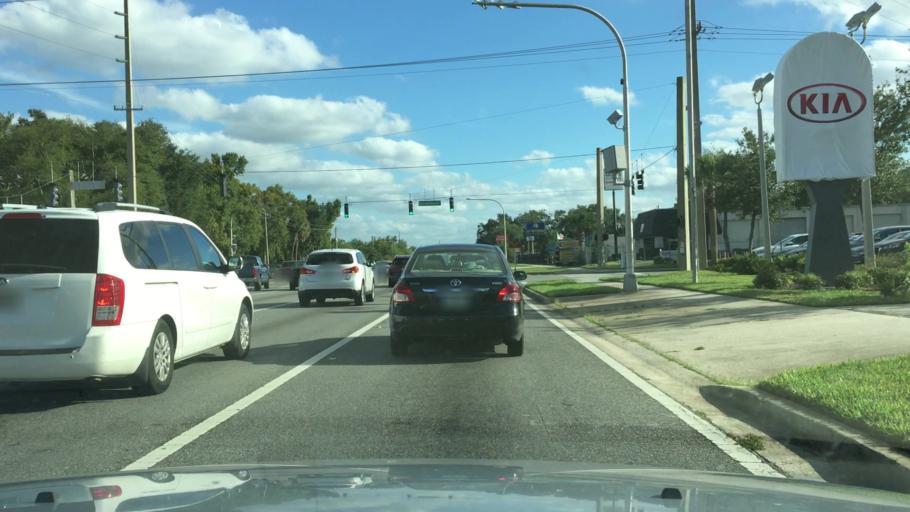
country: US
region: Florida
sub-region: Volusia County
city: Daytona Beach
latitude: 29.2114
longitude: -81.0442
